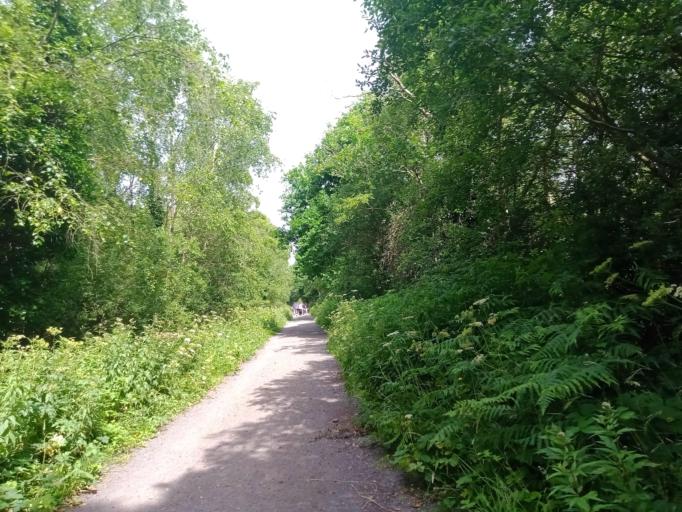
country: IE
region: Leinster
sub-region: Laois
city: Abbeyleix
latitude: 52.9019
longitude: -7.3507
